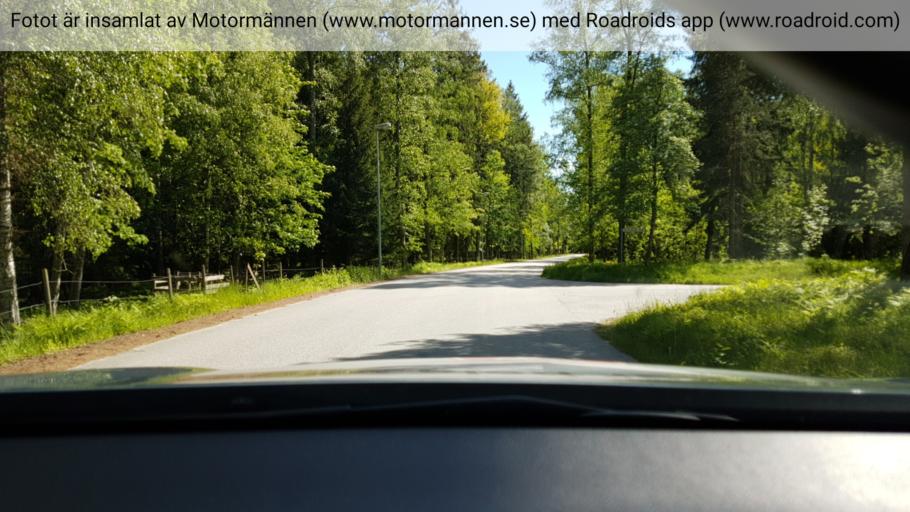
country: SE
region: Vaestra Goetaland
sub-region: Tibro Kommun
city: Tibro
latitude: 58.4245
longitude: 14.1463
